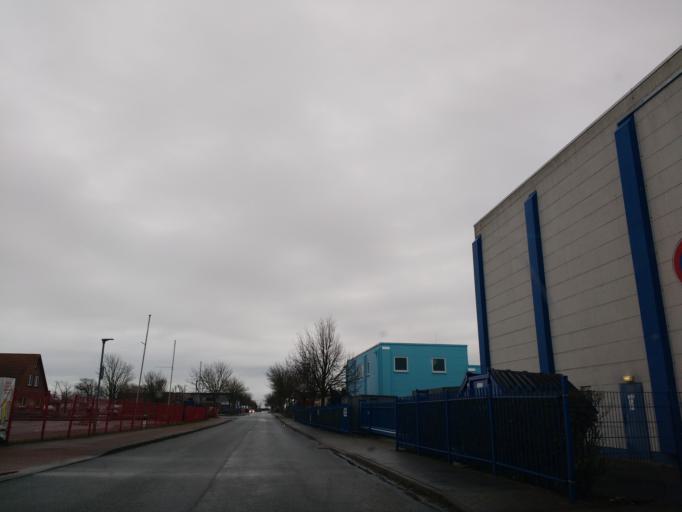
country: DE
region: Schleswig-Holstein
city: Fehmarn
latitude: 54.4461
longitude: 11.1813
